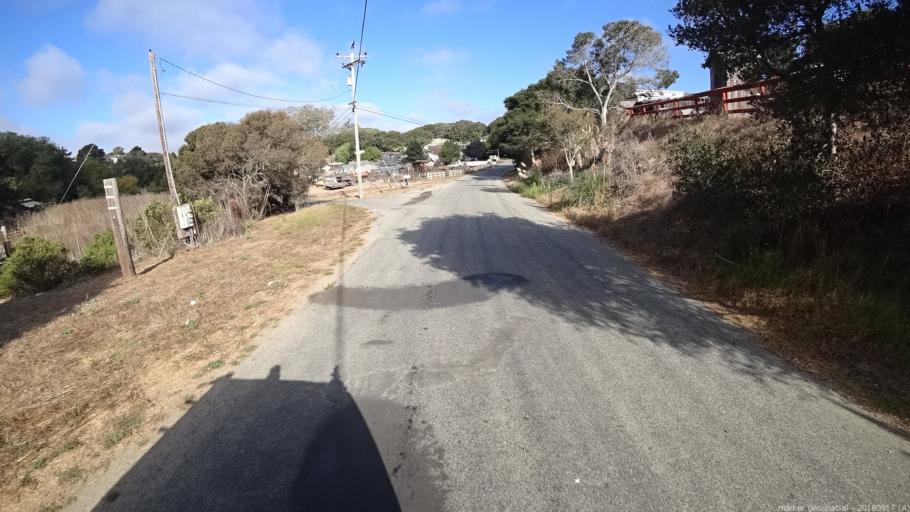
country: US
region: California
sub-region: Monterey County
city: Prunedale
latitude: 36.7895
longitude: -121.6850
